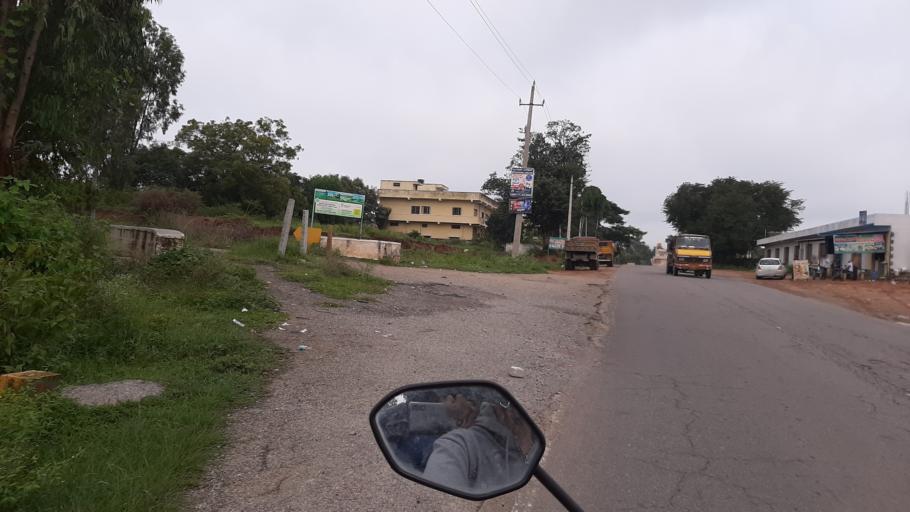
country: IN
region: Karnataka
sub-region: Bangalore Rural
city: Nelamangala
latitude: 12.9650
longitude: 77.3827
